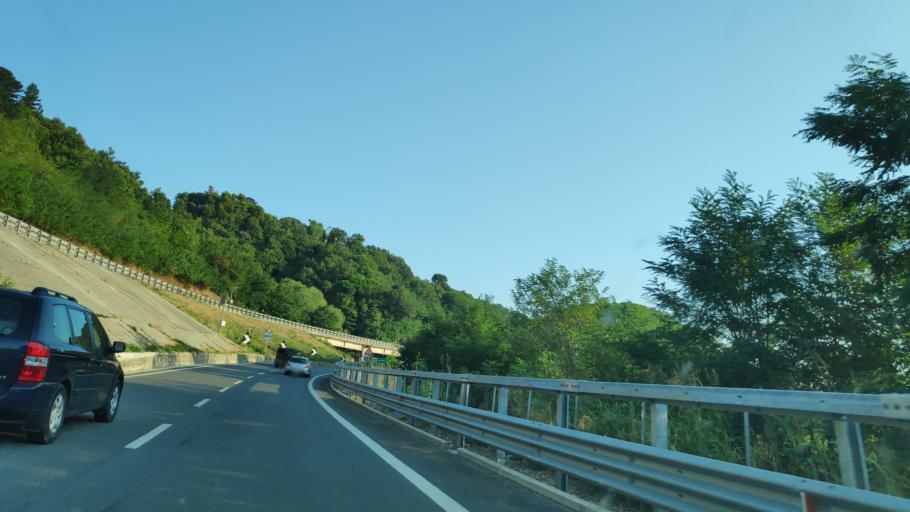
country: IT
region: Calabria
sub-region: Provincia di Cosenza
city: Belsito
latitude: 39.1691
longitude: 16.2929
